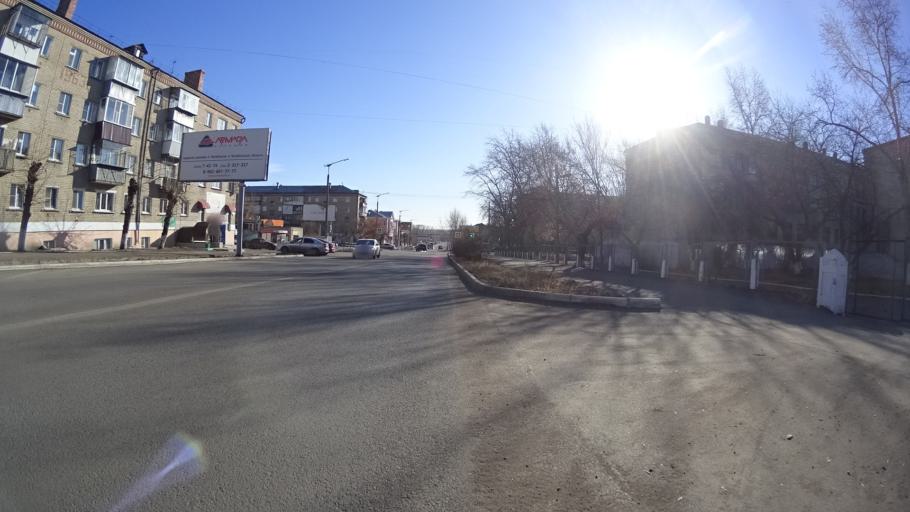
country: RU
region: Chelyabinsk
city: Troitsk
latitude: 54.0800
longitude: 61.5365
